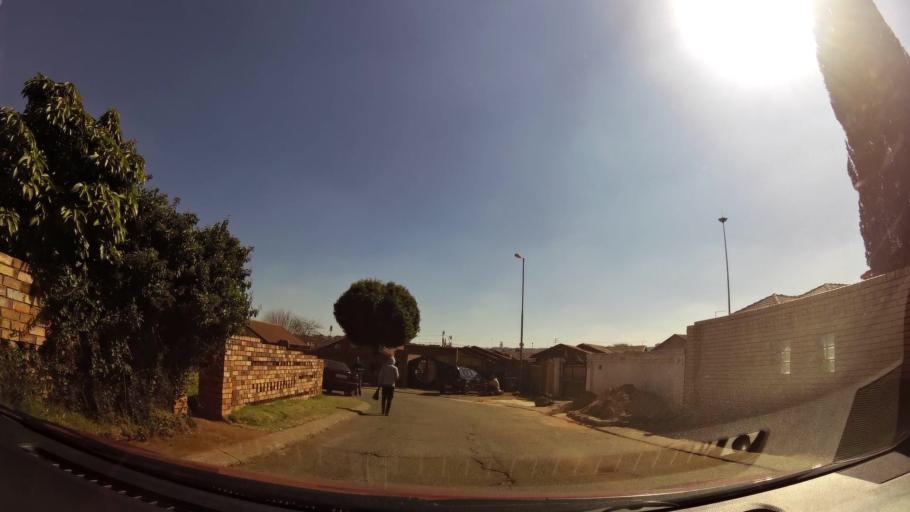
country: ZA
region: Gauteng
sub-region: City of Johannesburg Metropolitan Municipality
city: Soweto
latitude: -26.2376
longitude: 27.8188
